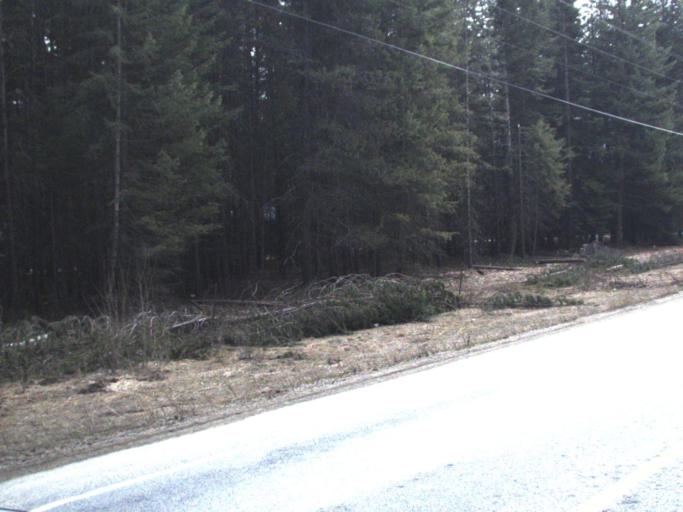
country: US
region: Washington
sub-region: Pend Oreille County
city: Newport
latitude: 48.2671
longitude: -117.2584
